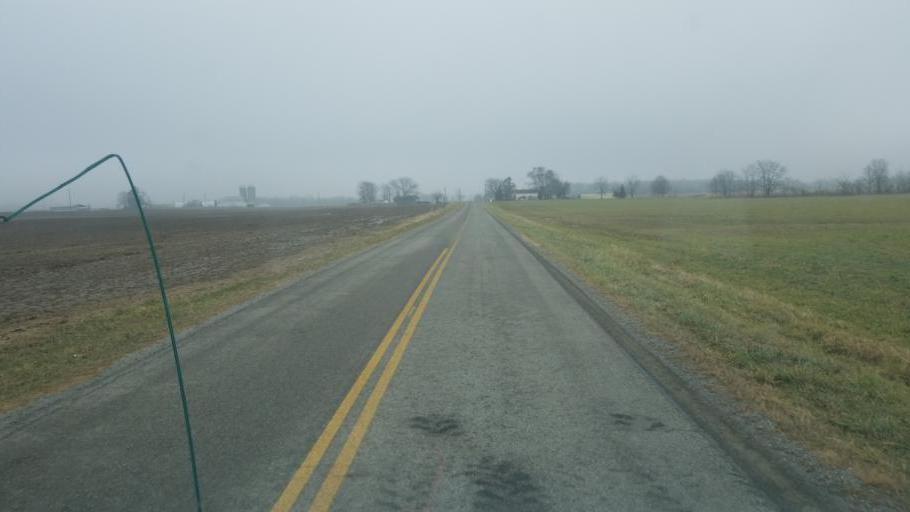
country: US
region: Ohio
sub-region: Champaign County
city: North Lewisburg
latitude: 40.3675
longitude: -83.5485
